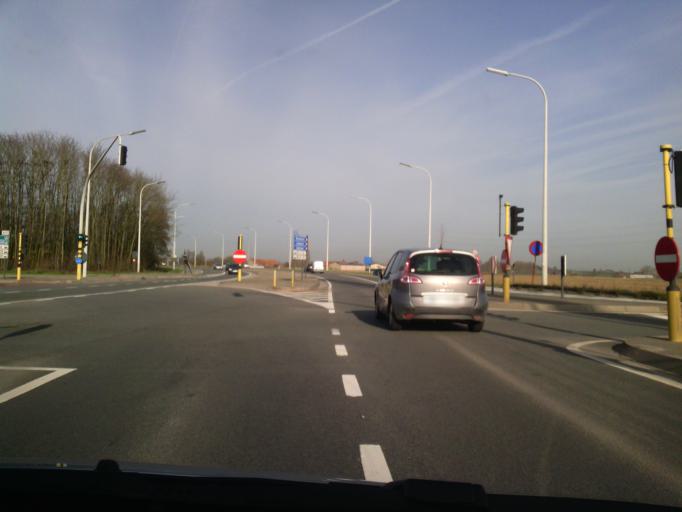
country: BE
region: Flanders
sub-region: Provincie West-Vlaanderen
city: Menen
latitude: 50.8172
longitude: 3.1260
